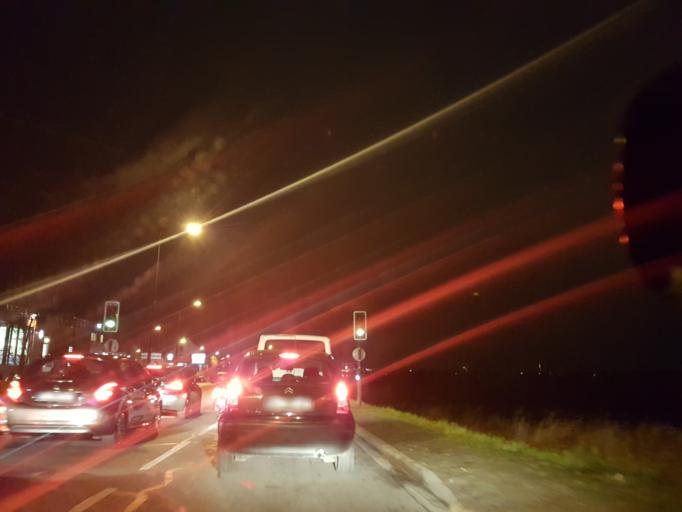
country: FR
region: Ile-de-France
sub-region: Departement des Yvelines
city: Chambourcy
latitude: 48.9070
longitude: 2.0483
